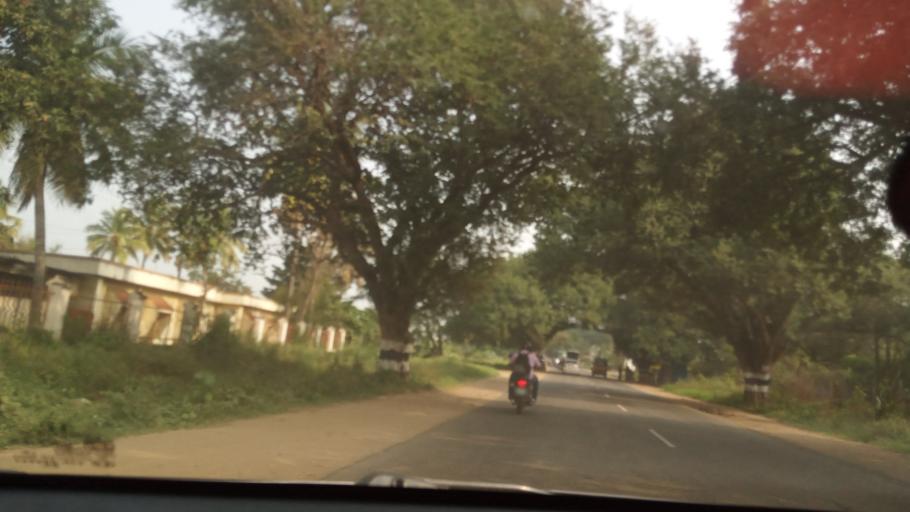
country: IN
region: Tamil Nadu
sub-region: Coimbatore
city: Annur
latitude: 11.1654
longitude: 77.0524
